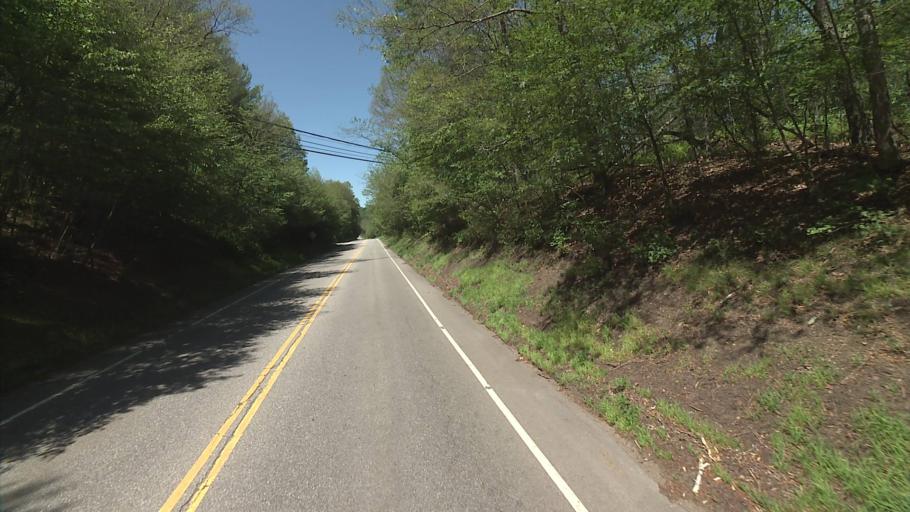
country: US
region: Connecticut
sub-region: New London County
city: Colchester
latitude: 41.5494
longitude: -72.3940
